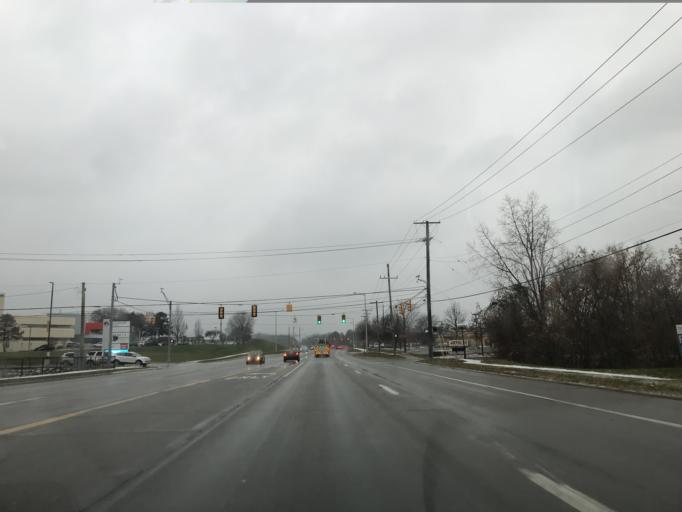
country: US
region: Michigan
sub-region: Wayne County
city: Northville
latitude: 42.4250
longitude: -83.4293
